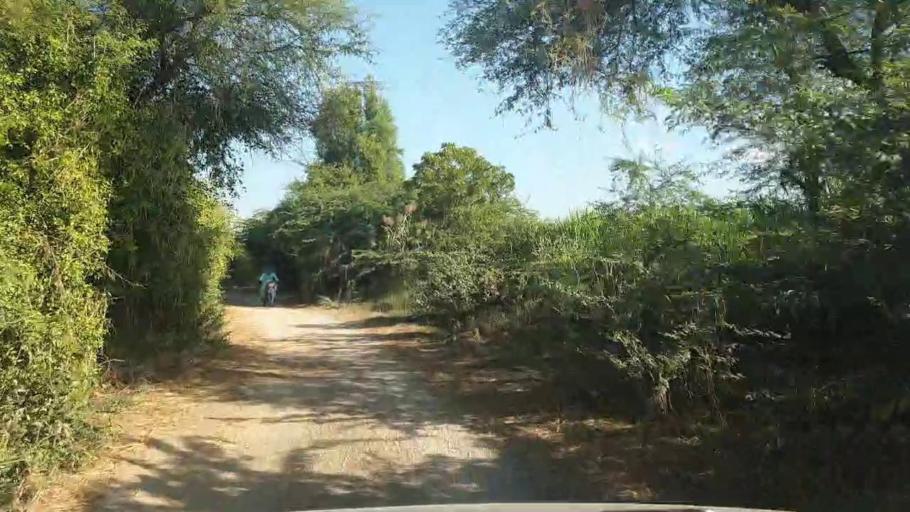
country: PK
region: Sindh
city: Talhar
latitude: 24.8273
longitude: 68.8198
